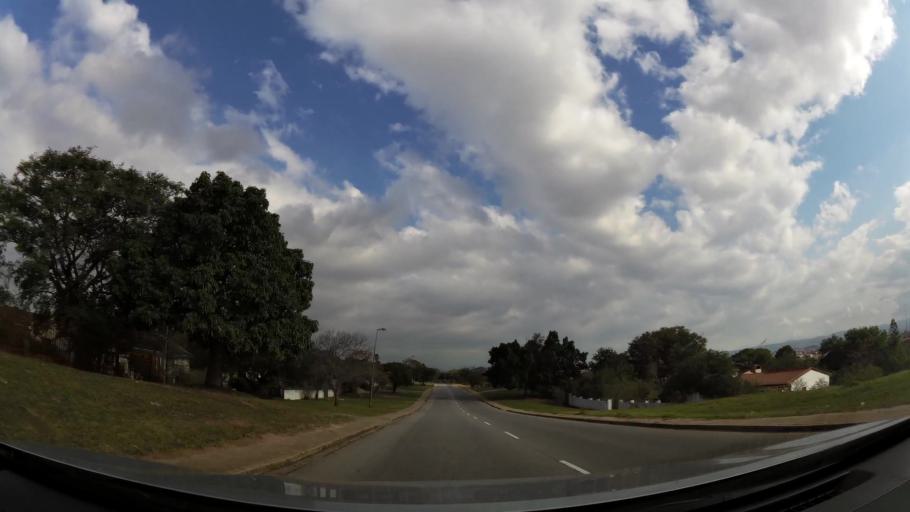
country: ZA
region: Eastern Cape
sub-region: Nelson Mandela Bay Metropolitan Municipality
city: Uitenhage
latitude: -33.7360
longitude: 25.4063
